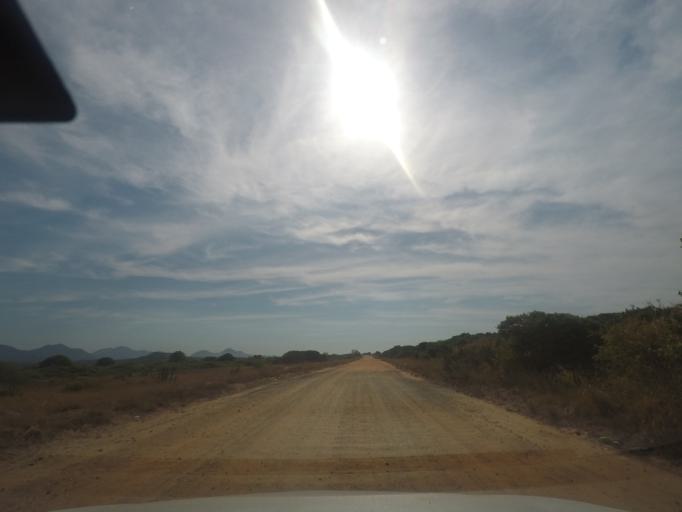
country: BR
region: Rio de Janeiro
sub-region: Marica
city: Marica
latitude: -22.9602
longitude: -42.8447
